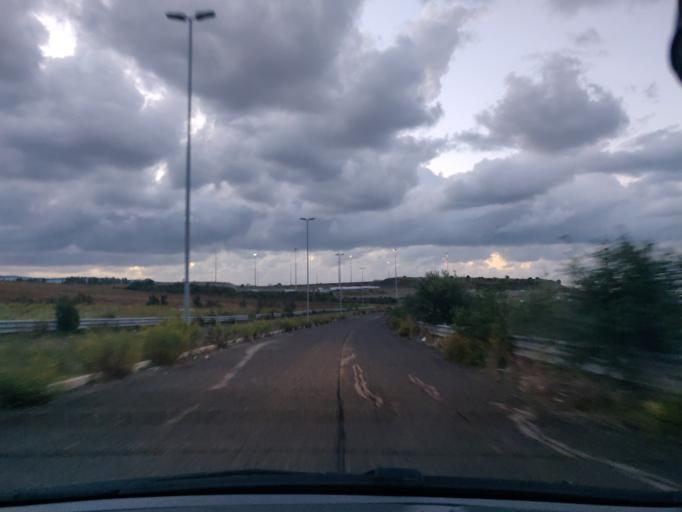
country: IT
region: Latium
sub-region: Citta metropolitana di Roma Capitale
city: Aurelia
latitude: 42.1316
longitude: 11.7767
